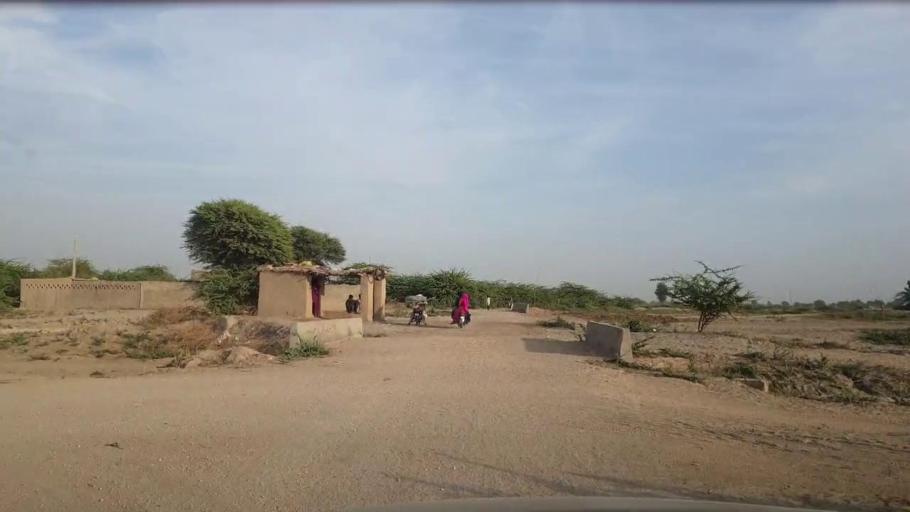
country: PK
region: Sindh
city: Kunri
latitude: 25.2247
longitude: 69.5146
